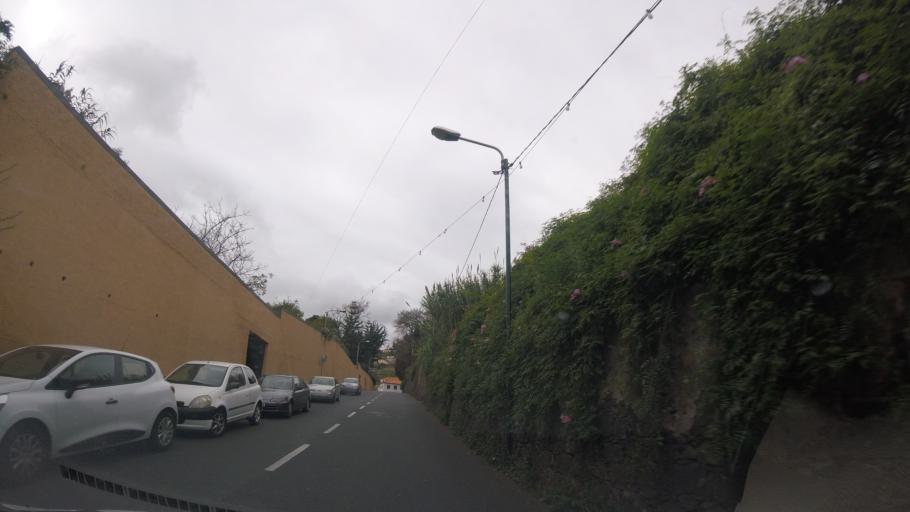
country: PT
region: Madeira
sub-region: Funchal
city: Nossa Senhora do Monte
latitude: 32.6558
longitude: -16.9338
